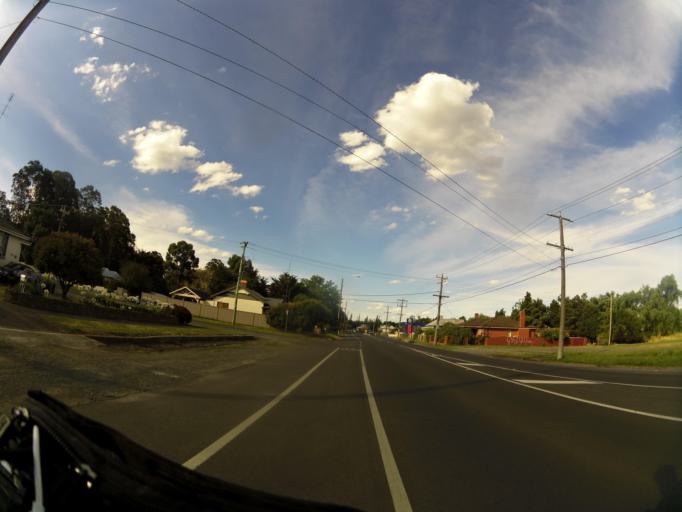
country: AU
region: Victoria
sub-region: Ballarat North
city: Golden Point
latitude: -37.5735
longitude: 143.8695
